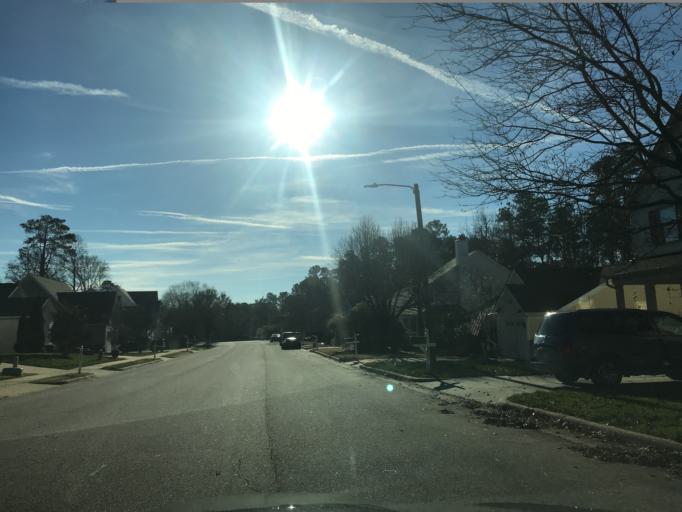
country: US
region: North Carolina
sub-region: Wake County
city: West Raleigh
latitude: 35.8902
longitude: -78.5985
